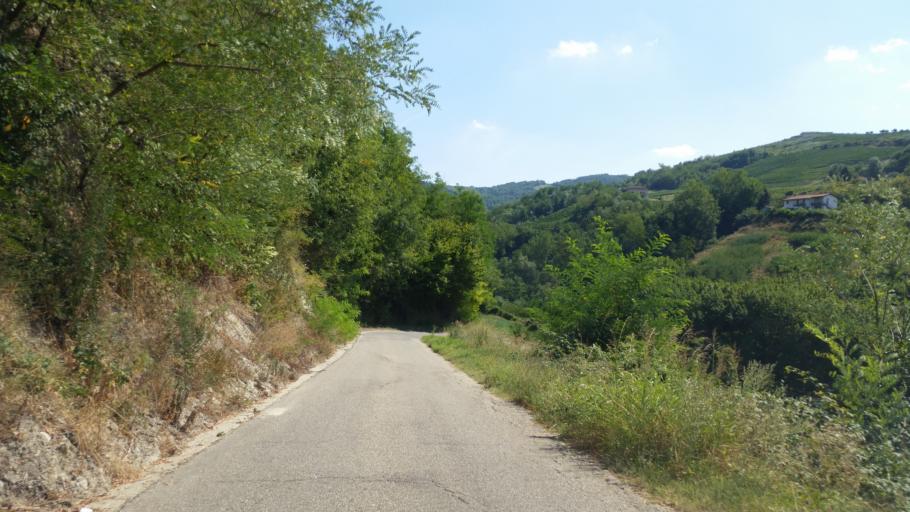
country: IT
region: Piedmont
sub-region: Provincia di Cuneo
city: Trezzo Tinella
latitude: 44.6755
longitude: 8.1144
